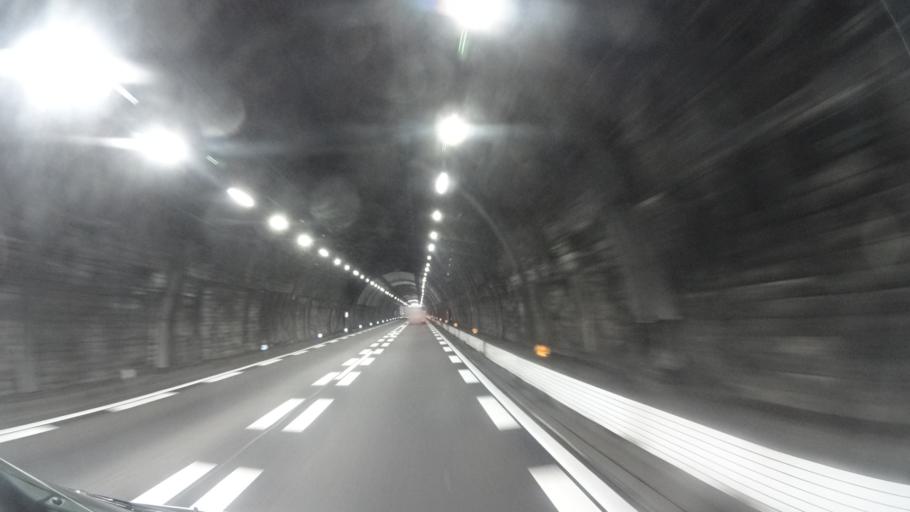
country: JP
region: Shiga Prefecture
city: Hikone
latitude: 35.2861
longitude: 136.2938
